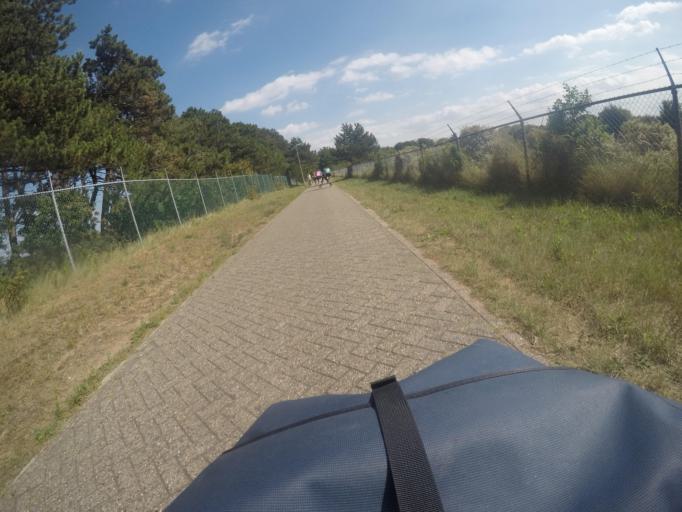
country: NL
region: North Holland
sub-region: Gemeente Zandvoort
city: Zandvoort
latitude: 52.3686
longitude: 4.5550
